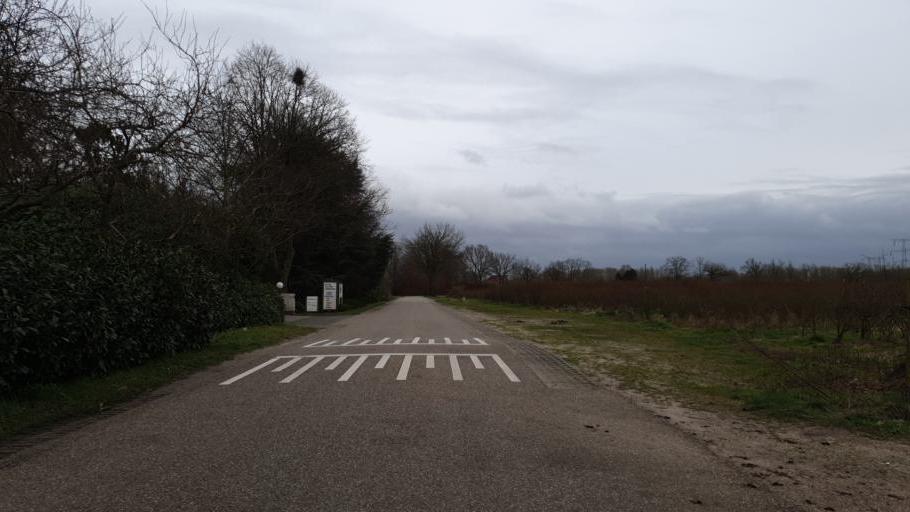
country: NL
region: North Brabant
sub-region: Gemeente Eindhoven
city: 't Hofke
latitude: 51.4657
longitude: 5.5229
